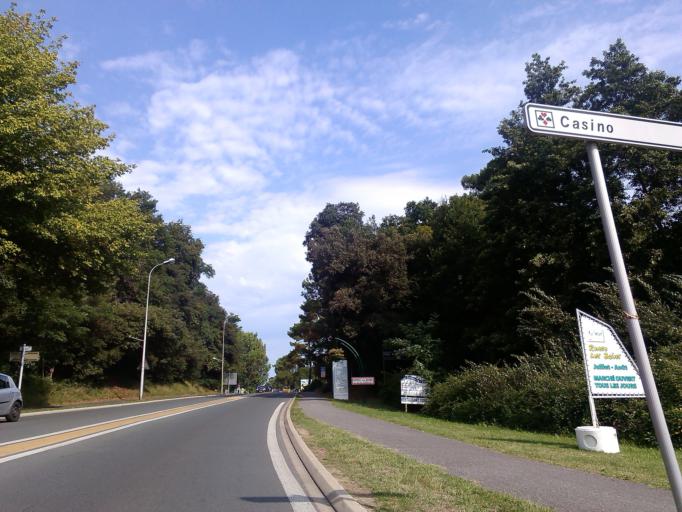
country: FR
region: Poitou-Charentes
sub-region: Departement de la Charente-Maritime
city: La Tremblade
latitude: 45.7860
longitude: -1.1575
